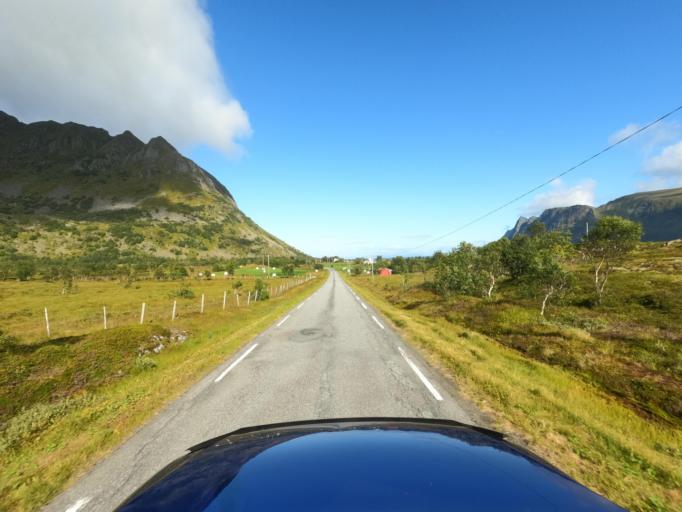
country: NO
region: Nordland
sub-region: Vagan
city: Kabelvag
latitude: 68.2885
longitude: 14.2659
